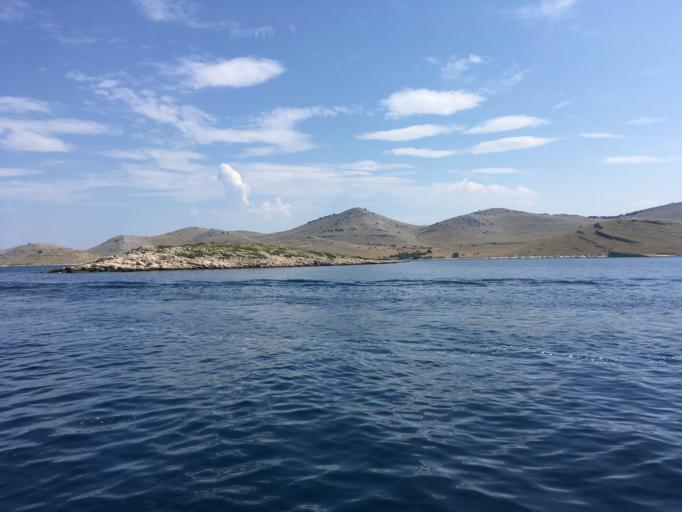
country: HR
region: Zadarska
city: Sali
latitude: 43.8357
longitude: 15.2388
